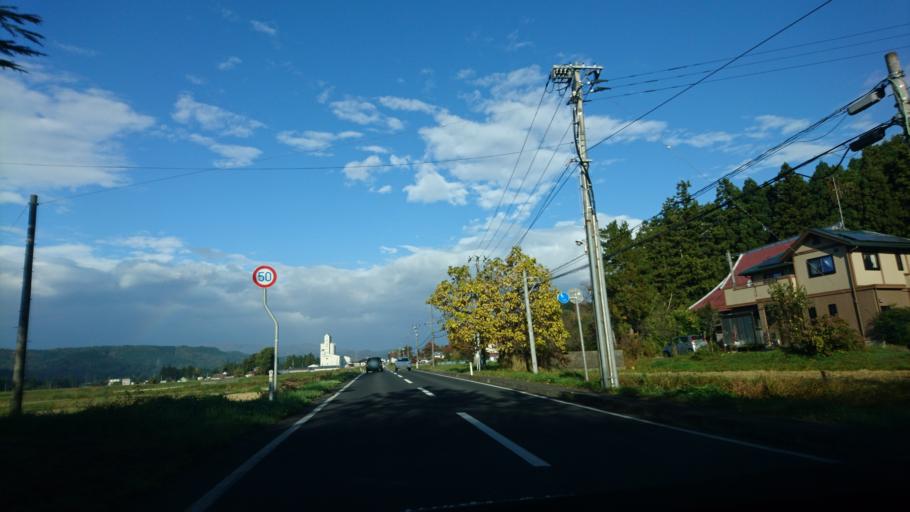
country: JP
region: Iwate
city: Ichinoseki
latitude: 39.0172
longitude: 141.1000
